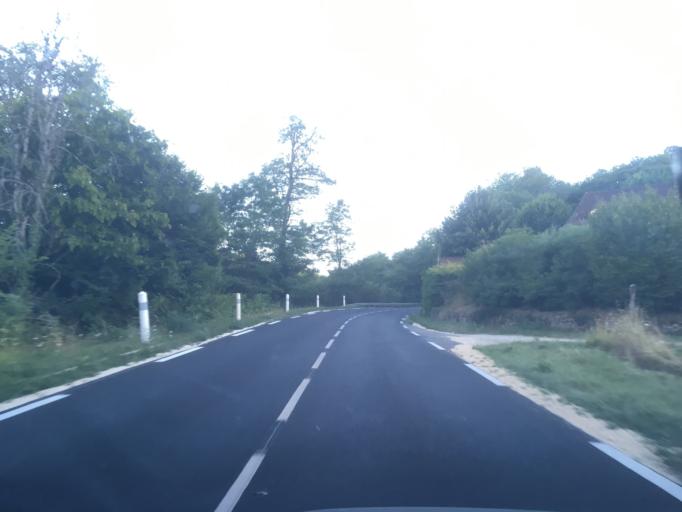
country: FR
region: Aquitaine
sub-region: Departement de la Dordogne
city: Sarlat-la-Caneda
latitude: 44.8647
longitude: 1.2024
